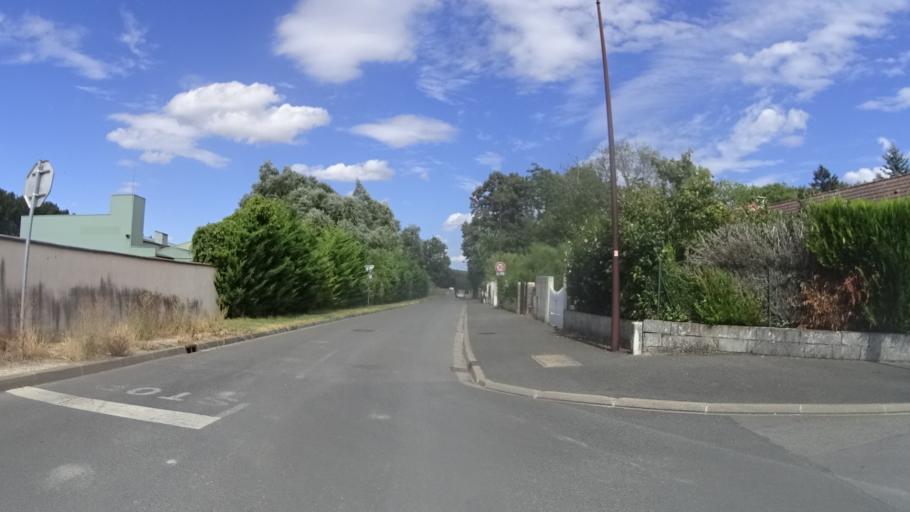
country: FR
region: Ile-de-France
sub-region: Departement de l'Essonne
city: Maisse
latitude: 48.3974
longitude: 2.3981
